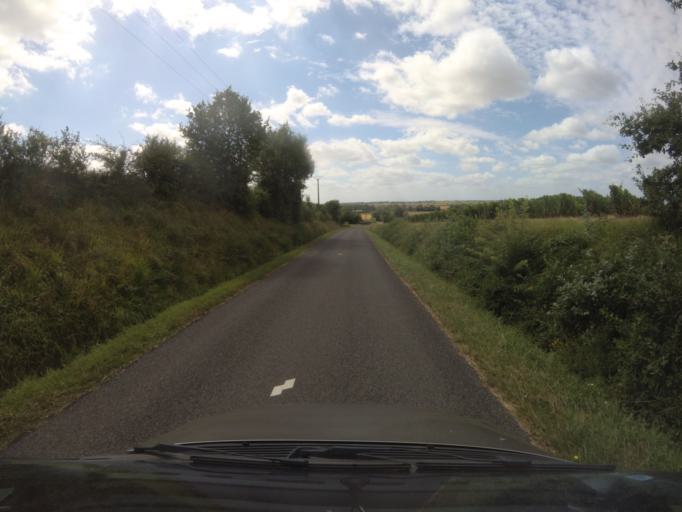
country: FR
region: Pays de la Loire
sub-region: Departement de Maine-et-Loire
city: Nueil-sur-Layon
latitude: 47.1836
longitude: -0.3524
